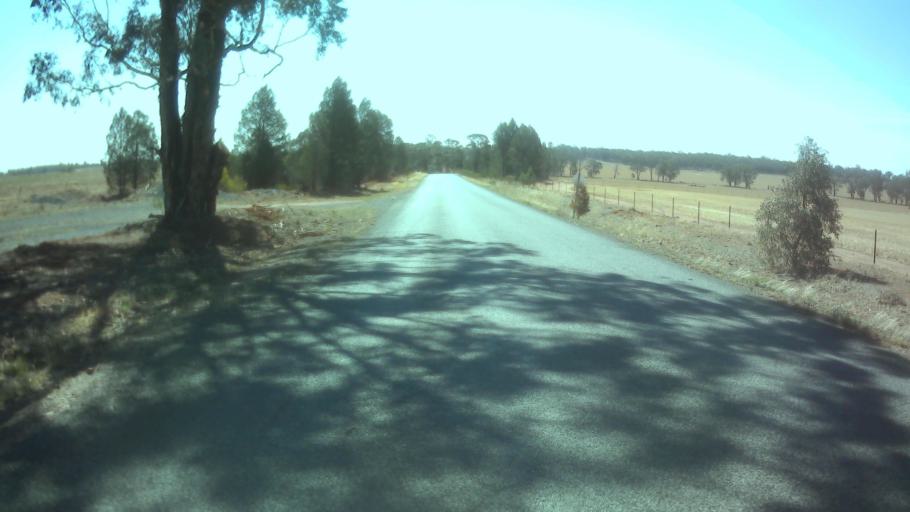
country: AU
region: New South Wales
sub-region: Weddin
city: Grenfell
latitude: -33.7562
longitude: 147.8542
